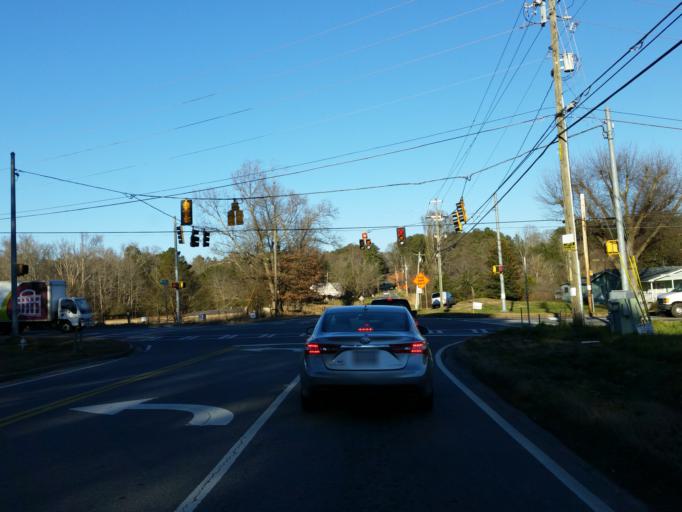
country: US
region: Georgia
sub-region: Cherokee County
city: Woodstock
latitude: 34.1145
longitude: -84.4592
